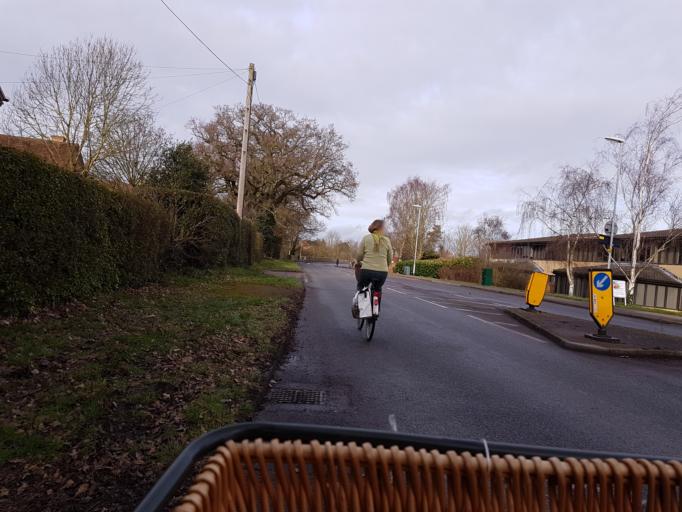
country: GB
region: England
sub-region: Cambridgeshire
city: Girton
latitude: 52.2312
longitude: 0.0863
